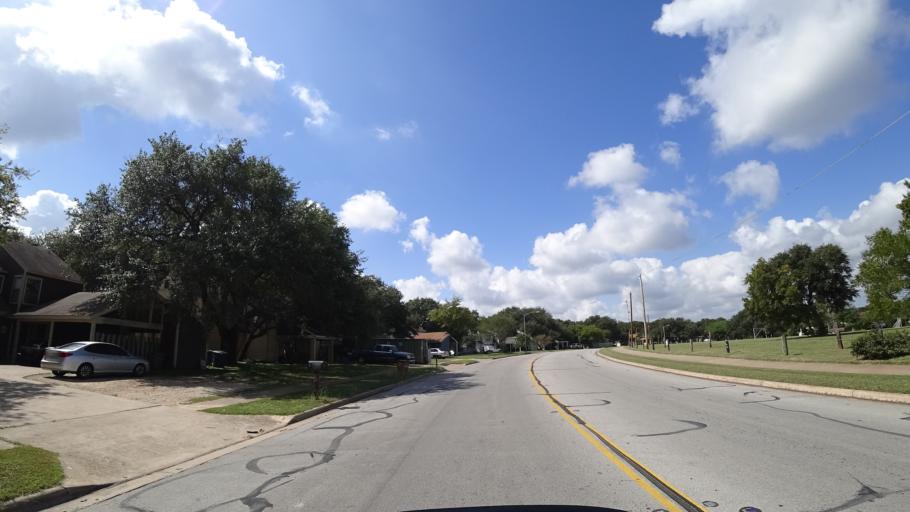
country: US
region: Texas
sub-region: Travis County
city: Onion Creek
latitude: 30.1991
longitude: -97.7997
